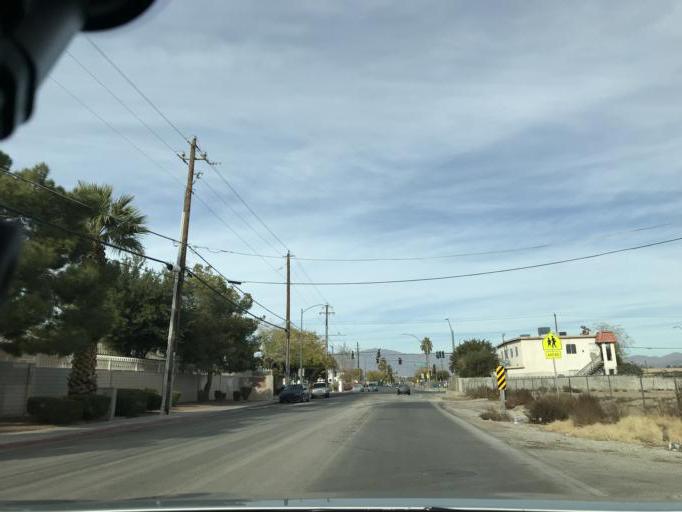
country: US
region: Nevada
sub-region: Clark County
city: Las Vegas
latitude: 36.1800
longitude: -115.1700
